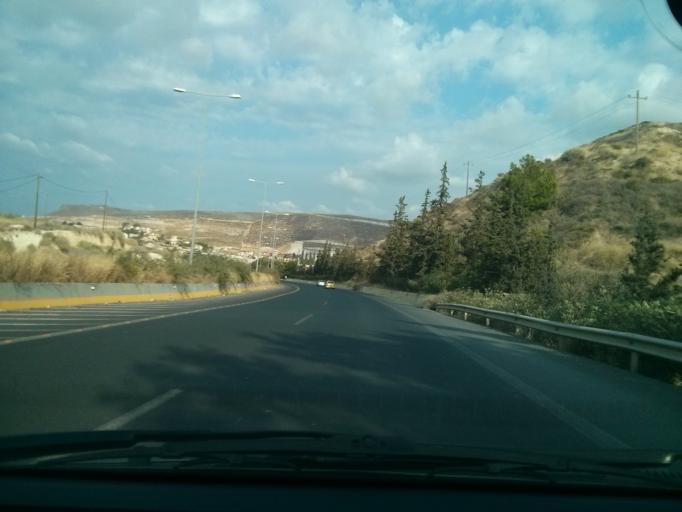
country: GR
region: Crete
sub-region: Nomos Irakleiou
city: Nea Alikarnassos
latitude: 35.3211
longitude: 25.1874
